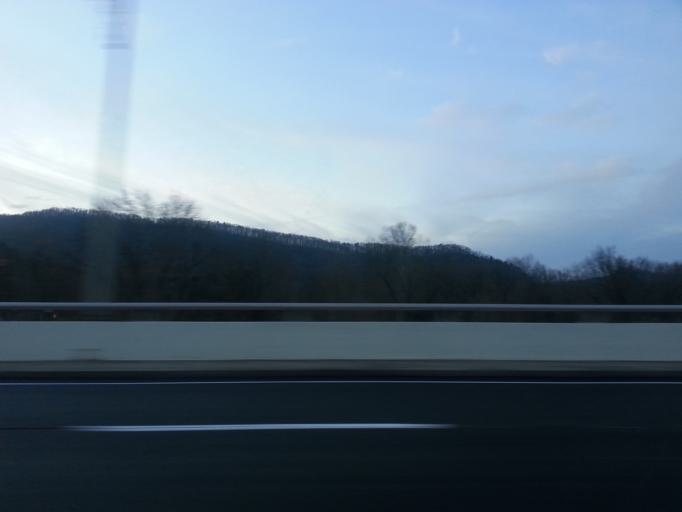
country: US
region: Tennessee
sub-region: Roane County
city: Harriman
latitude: 35.9305
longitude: -84.5557
